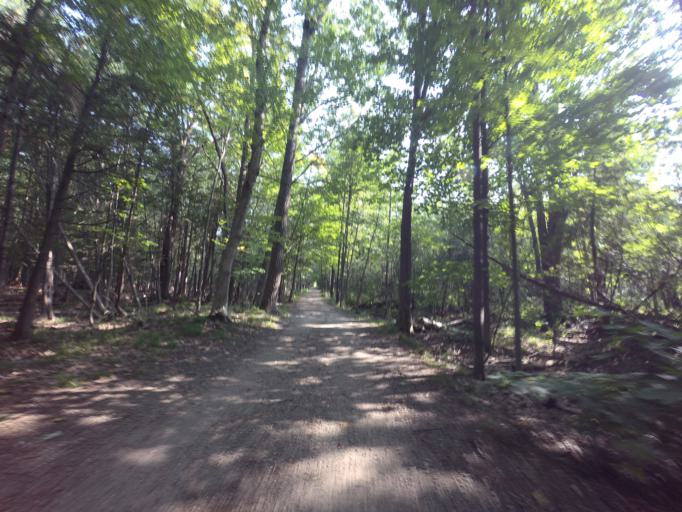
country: CA
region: Ontario
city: Bells Corners
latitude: 45.2937
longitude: -75.8449
